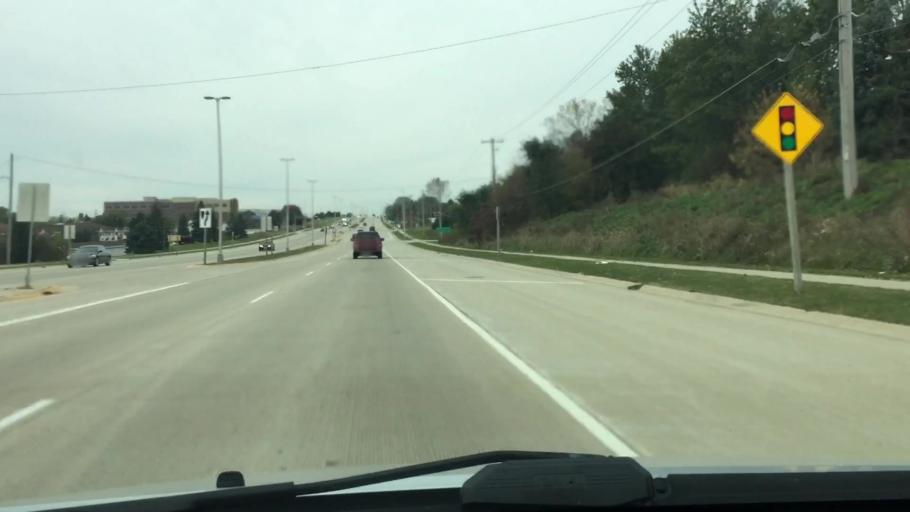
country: US
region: Wisconsin
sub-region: Milwaukee County
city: Greendale
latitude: 42.8728
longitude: -87.9633
